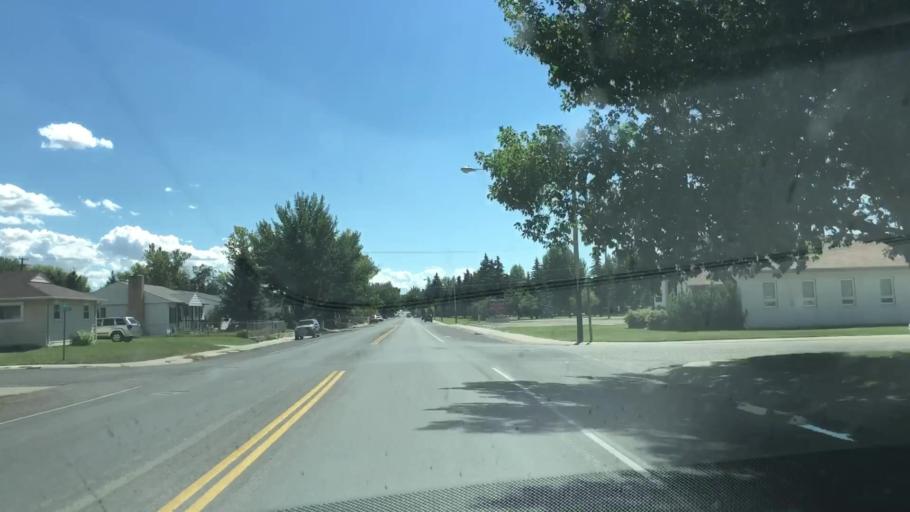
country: US
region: Wyoming
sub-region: Albany County
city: Laramie
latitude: 41.3240
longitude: -105.5843
